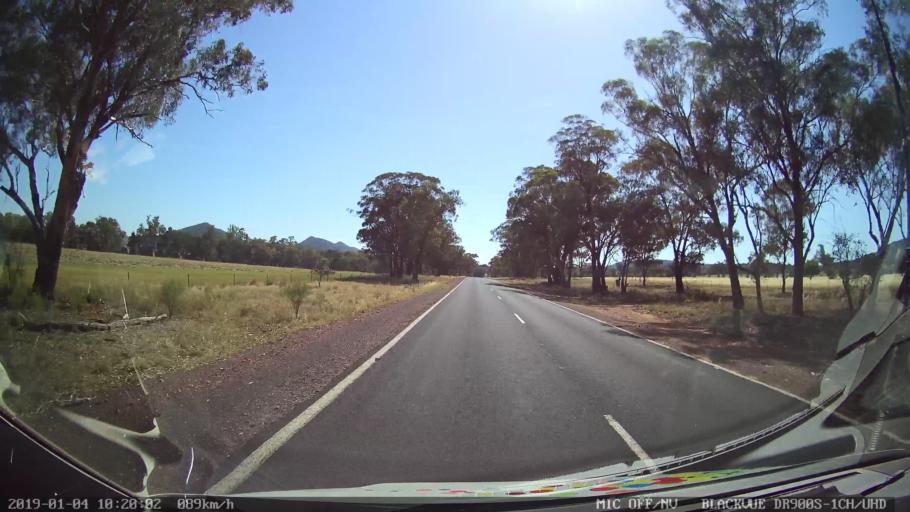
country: AU
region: New South Wales
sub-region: Cabonne
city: Canowindra
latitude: -33.3738
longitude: 148.4896
